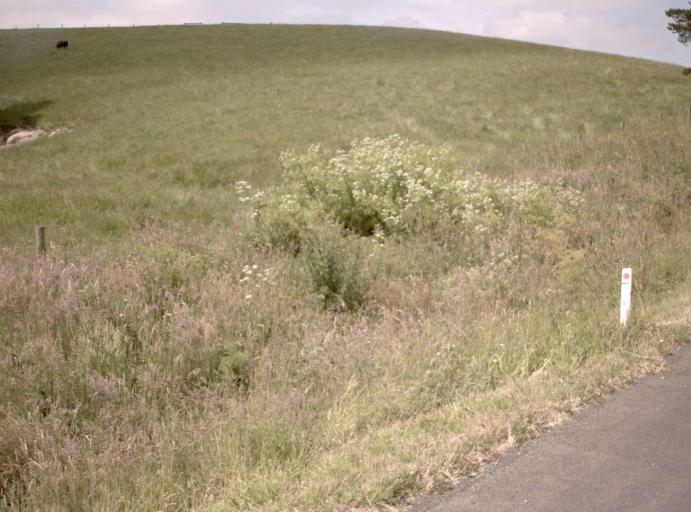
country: AU
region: Victoria
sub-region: Baw Baw
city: Warragul
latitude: -38.4117
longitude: 146.0474
